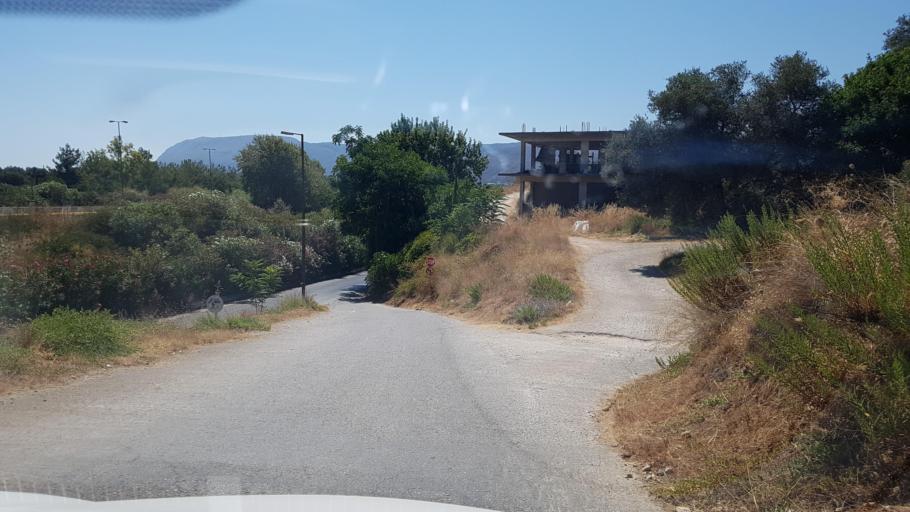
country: GR
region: Crete
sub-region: Nomos Chanias
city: Perivolia
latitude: 35.4986
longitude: 23.9911
